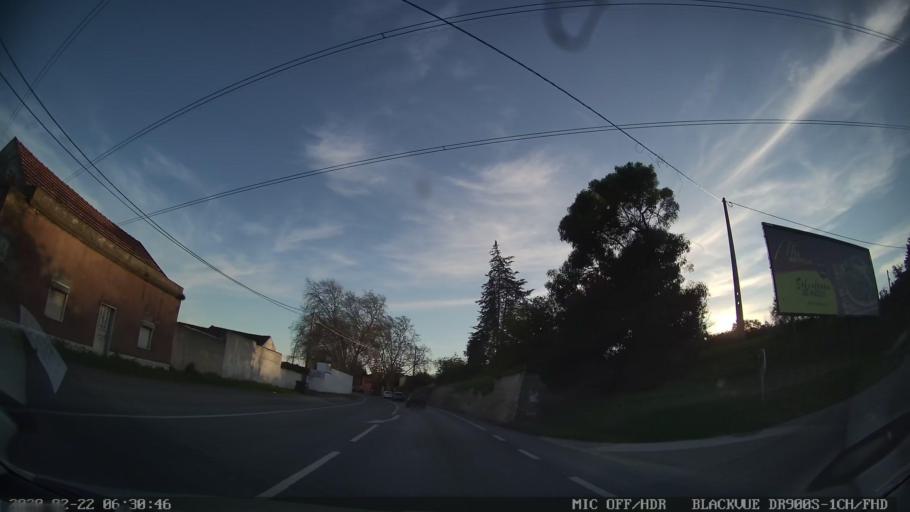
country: PT
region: Lisbon
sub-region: Vila Franca de Xira
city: Castanheira do Ribatejo
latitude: 38.9826
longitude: -8.9776
